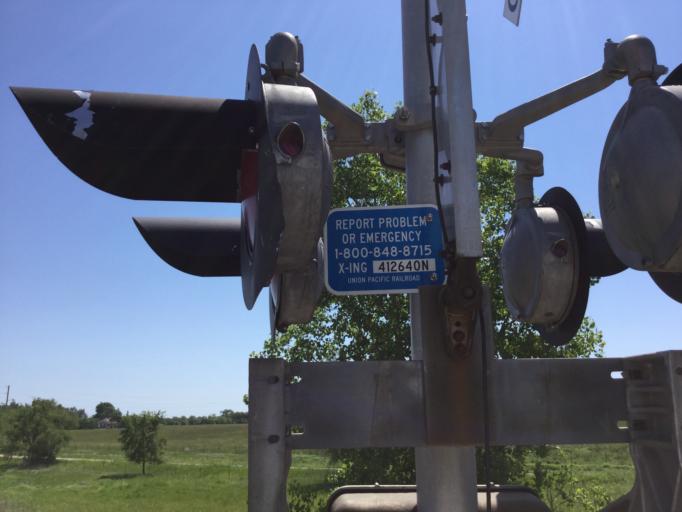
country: US
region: Kansas
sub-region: Anderson County
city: Garnett
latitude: 38.1385
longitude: -95.1227
